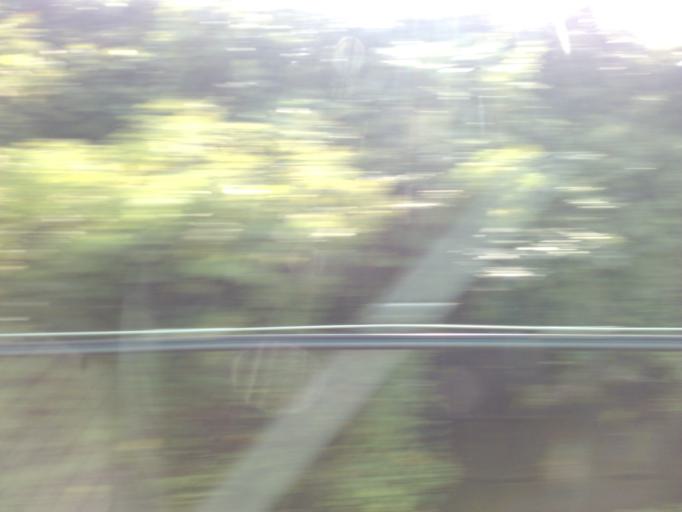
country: JP
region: Iwate
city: Ichinoseki
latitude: 38.8652
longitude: 141.1165
